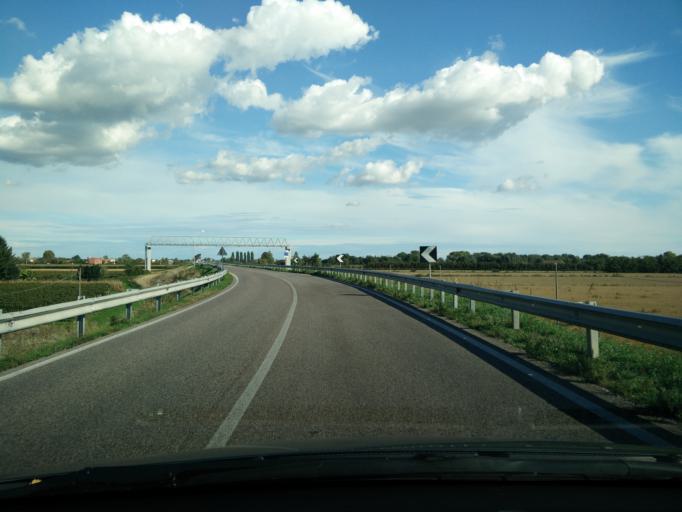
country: IT
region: Veneto
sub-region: Provincia di Treviso
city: Talponada
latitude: 45.6940
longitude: 12.4883
